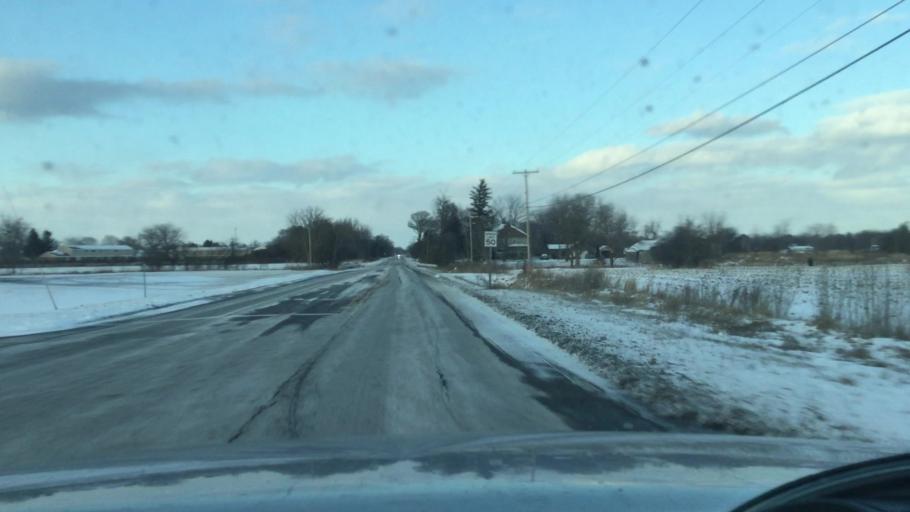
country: US
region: Michigan
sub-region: Saginaw County
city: Saginaw
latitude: 43.3769
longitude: -83.9354
